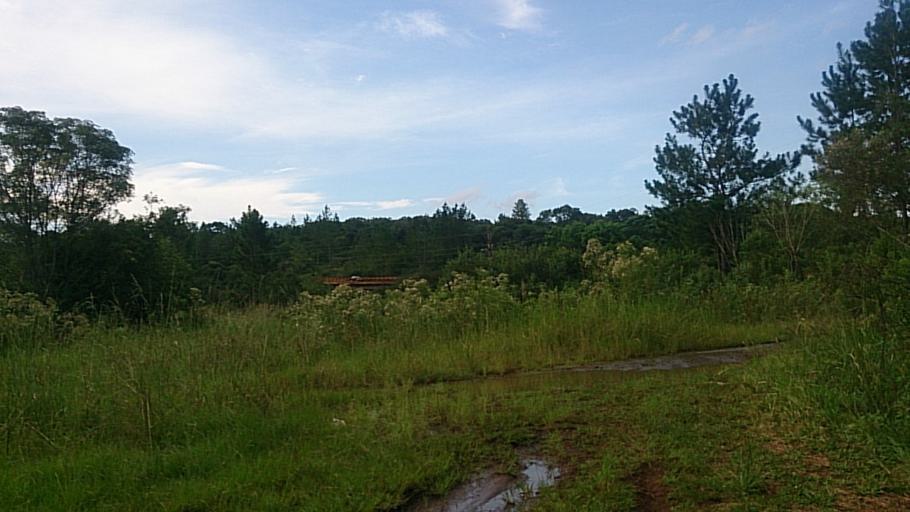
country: AR
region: Misiones
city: Campo Viera
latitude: -27.3678
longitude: -55.0483
